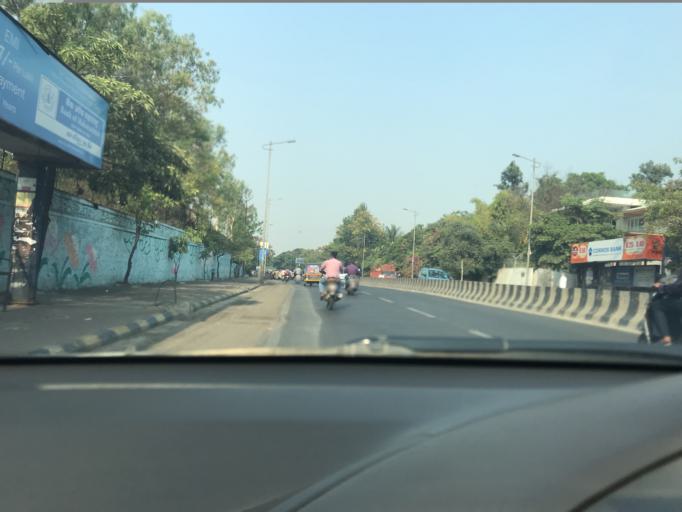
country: IN
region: Maharashtra
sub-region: Pune Division
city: Khadki
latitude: 18.5493
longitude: 73.8114
